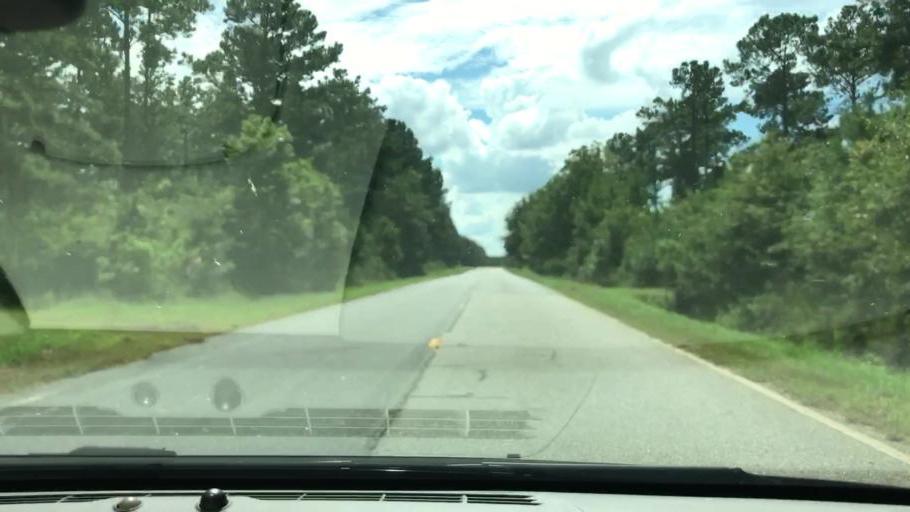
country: US
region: Georgia
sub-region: Quitman County
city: Georgetown
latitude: 32.0000
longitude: -85.0383
